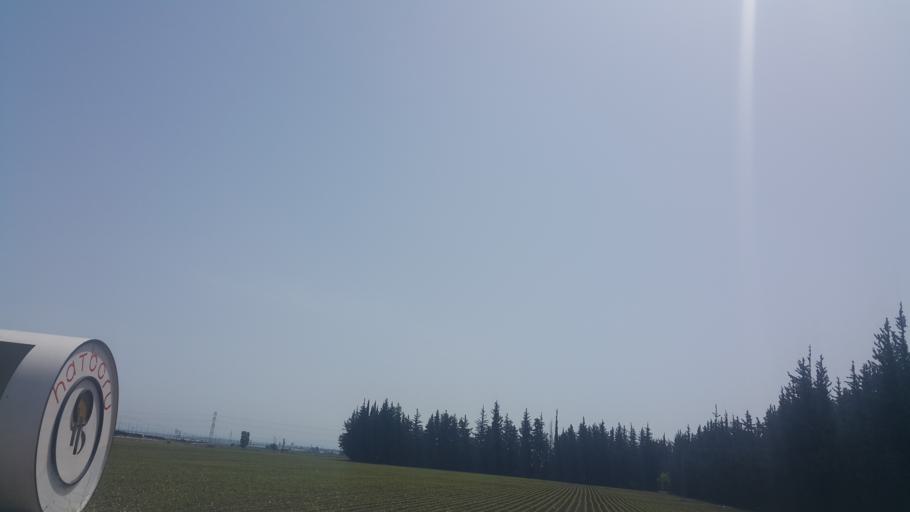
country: TR
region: Hatay
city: Serinyol
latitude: 36.3717
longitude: 36.2258
